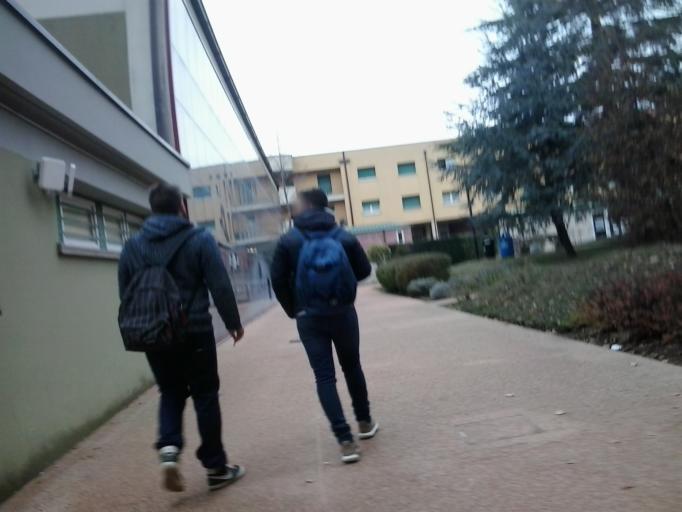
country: IT
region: Lombardy
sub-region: Provincia di Brescia
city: Bovezzo
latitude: 45.5647
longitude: 10.2351
